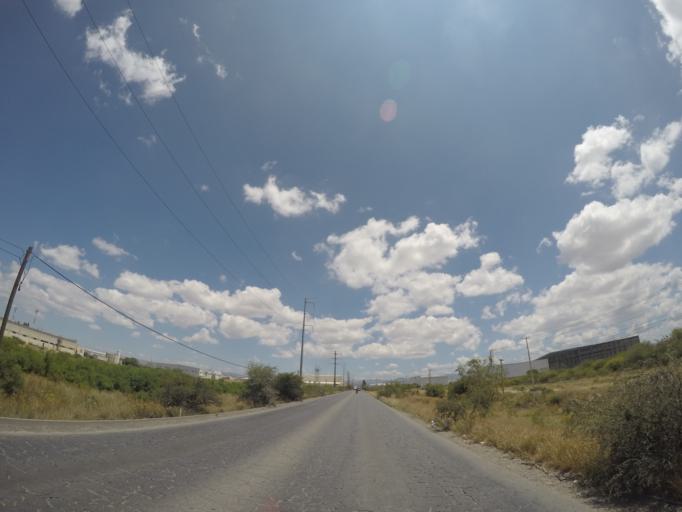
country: MX
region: San Luis Potosi
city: La Pila
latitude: 22.0461
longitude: -100.8763
